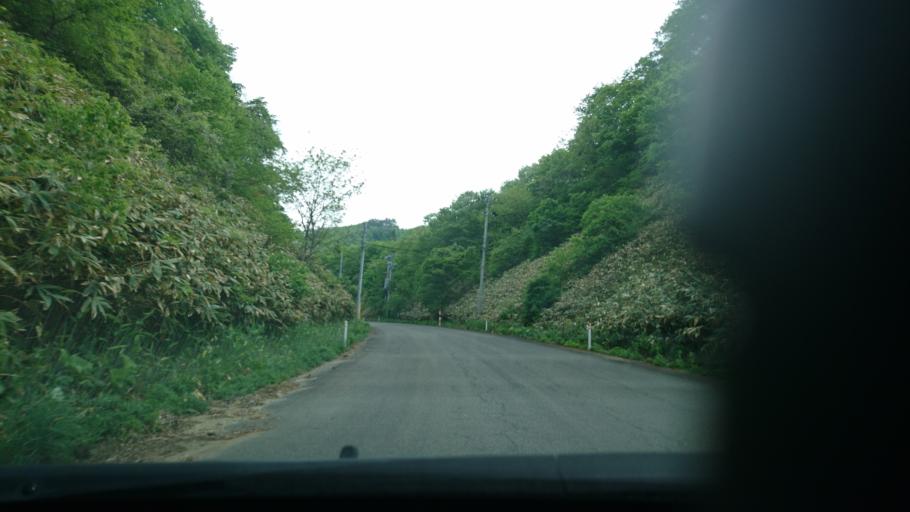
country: JP
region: Iwate
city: Ichinoseki
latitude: 38.8989
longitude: 140.9092
